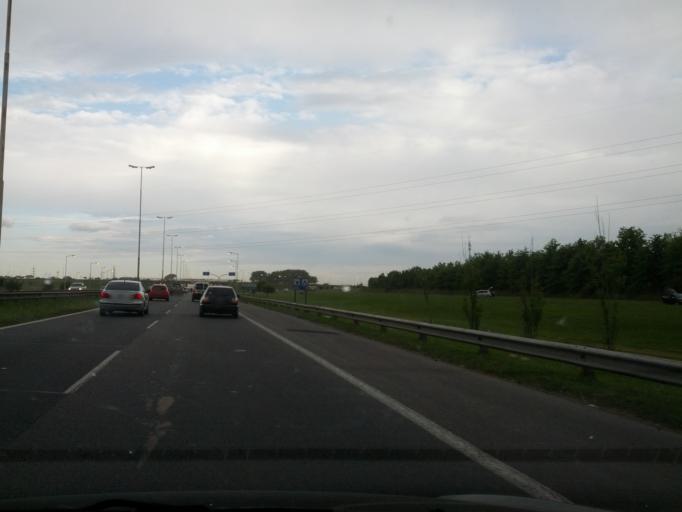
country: AR
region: Buenos Aires
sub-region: Partido de Lujan
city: Lujan
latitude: -34.5726
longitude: -59.0428
